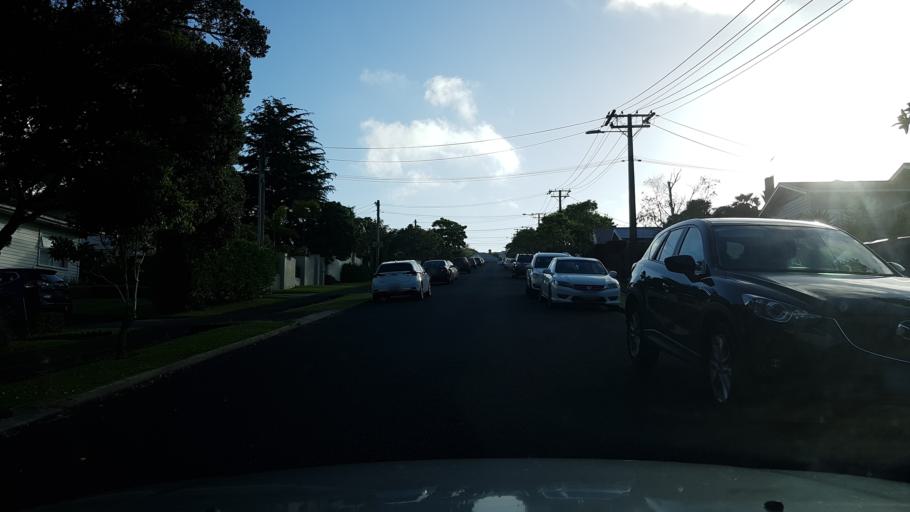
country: NZ
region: Auckland
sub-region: Auckland
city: North Shore
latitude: -36.8142
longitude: 174.7330
